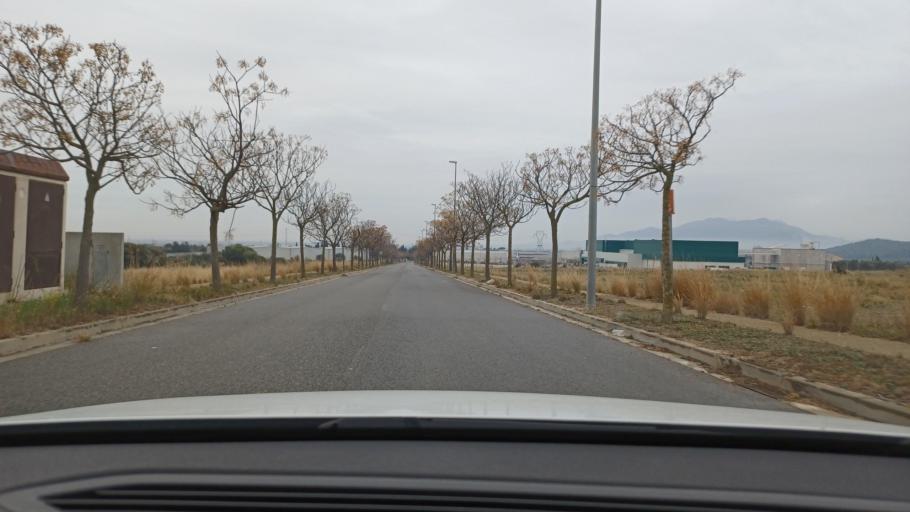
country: ES
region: Catalonia
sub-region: Provincia de Tarragona
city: Amposta
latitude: 40.7613
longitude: 0.5999
